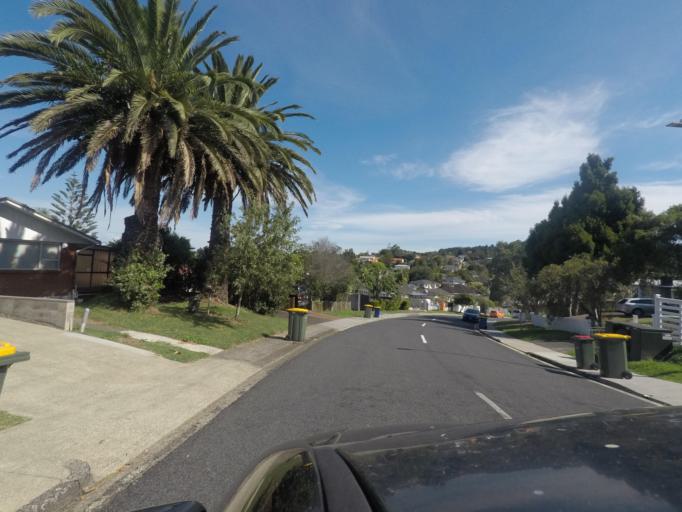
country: NZ
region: Auckland
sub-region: Auckland
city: Waitakere
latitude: -36.9280
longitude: 174.6685
